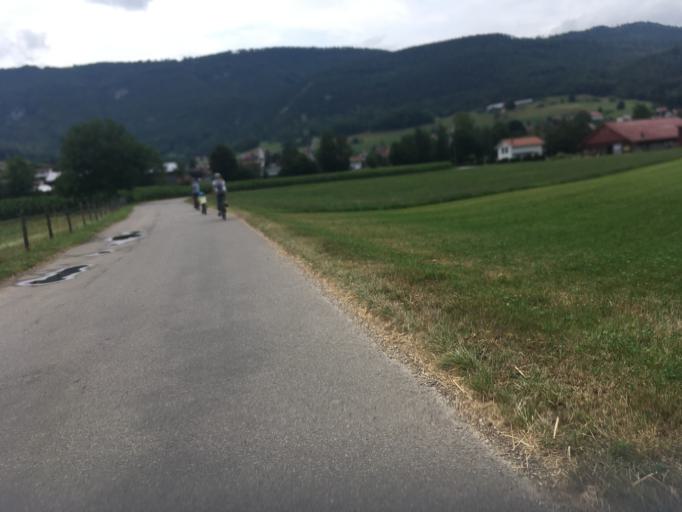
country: CH
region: Solothurn
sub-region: Bezirk Thal
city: Laupersdorf
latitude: 47.3074
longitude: 7.6533
